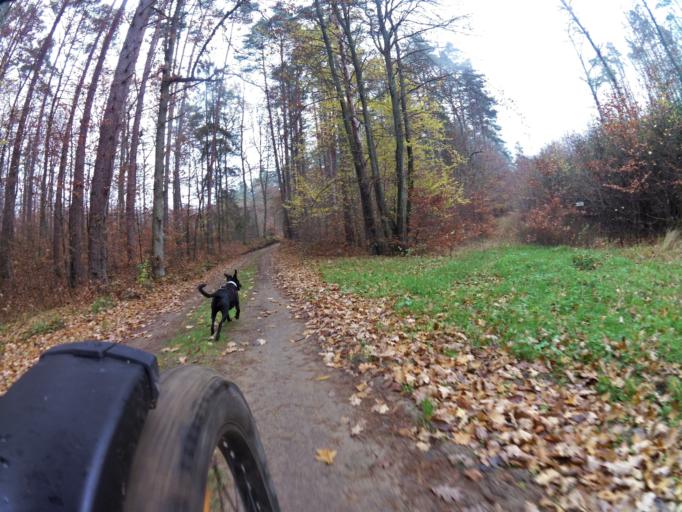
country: PL
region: Pomeranian Voivodeship
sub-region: Powiat wejherowski
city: Orle
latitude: 54.6954
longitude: 18.1564
